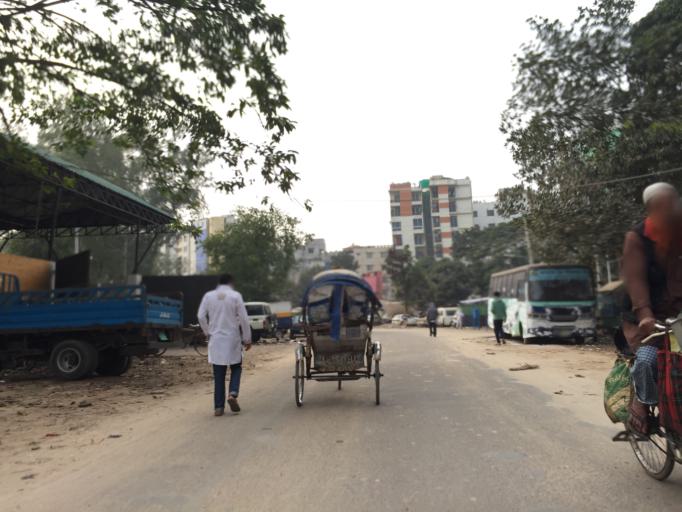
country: BD
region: Dhaka
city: Azimpur
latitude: 23.7802
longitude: 90.3722
